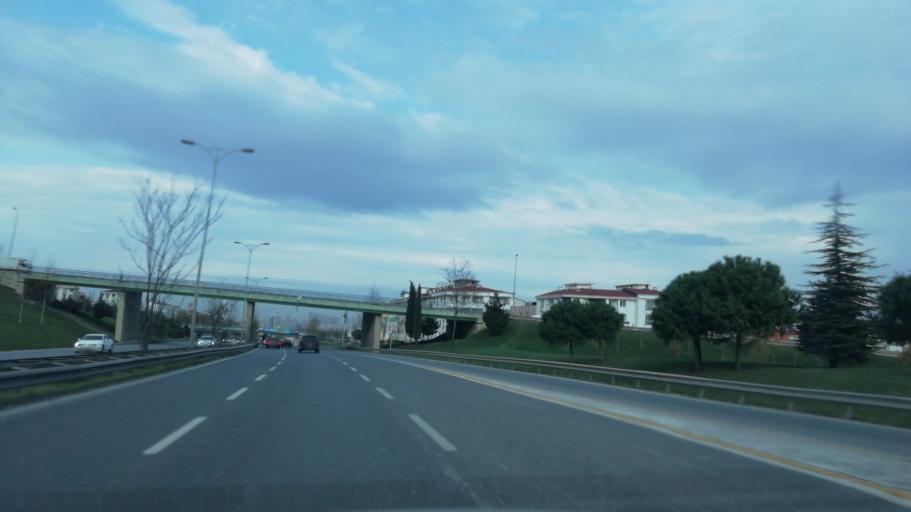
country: TR
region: Istanbul
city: Esenyurt
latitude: 41.0307
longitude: 28.6868
